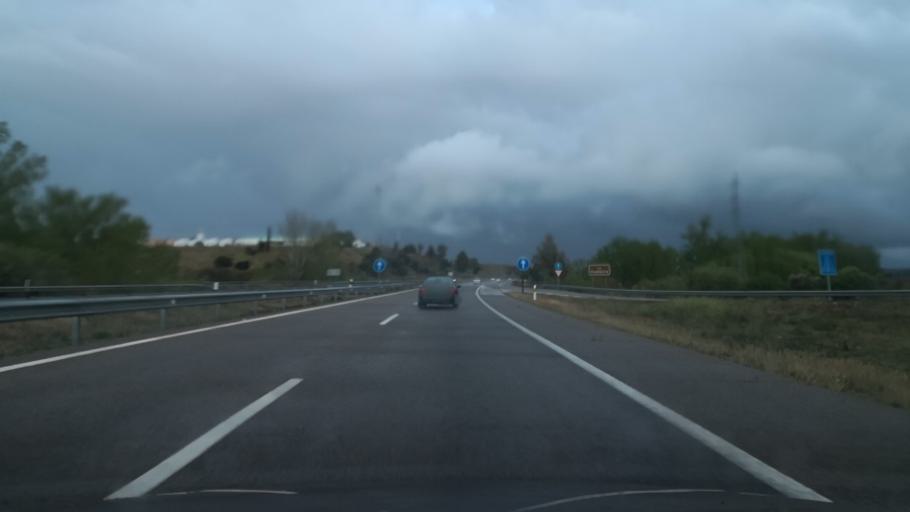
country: ES
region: Extremadura
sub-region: Provincia de Badajoz
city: Valdelacalzada
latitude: 38.8506
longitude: -6.6894
